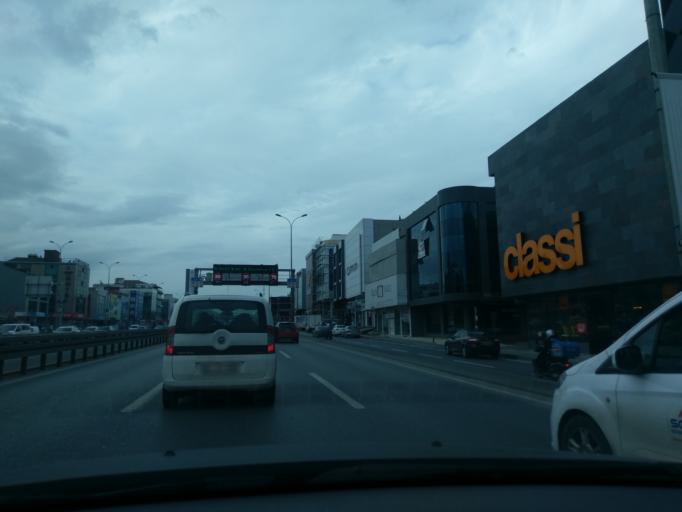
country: TR
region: Istanbul
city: Yakuplu
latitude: 40.9889
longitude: 28.7169
